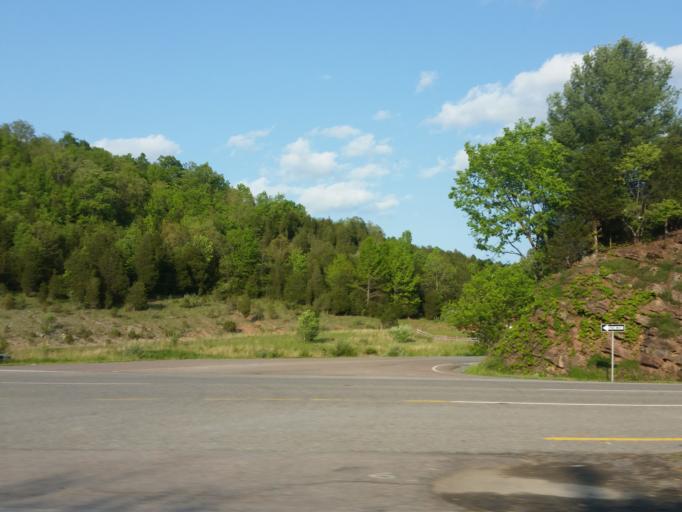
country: US
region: Virginia
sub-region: Tazewell County
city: Claypool Hill
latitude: 37.0132
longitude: -81.7948
